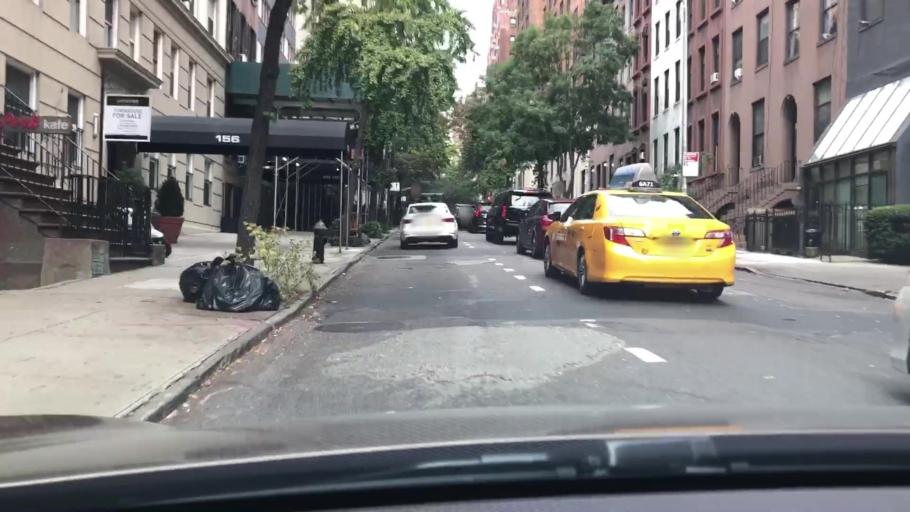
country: US
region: New York
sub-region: Queens County
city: Long Island City
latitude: 40.7478
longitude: -73.9772
